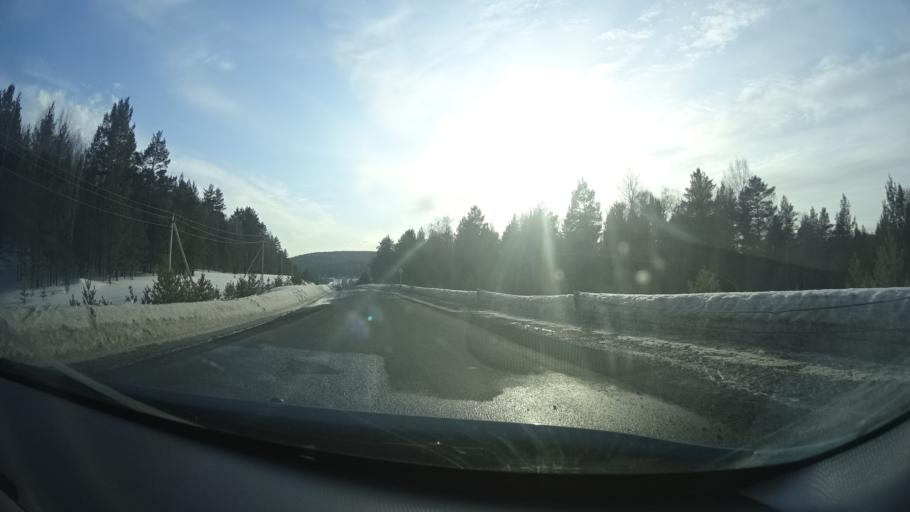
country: RU
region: Bashkortostan
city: Lomovka
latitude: 53.6712
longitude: 58.2274
